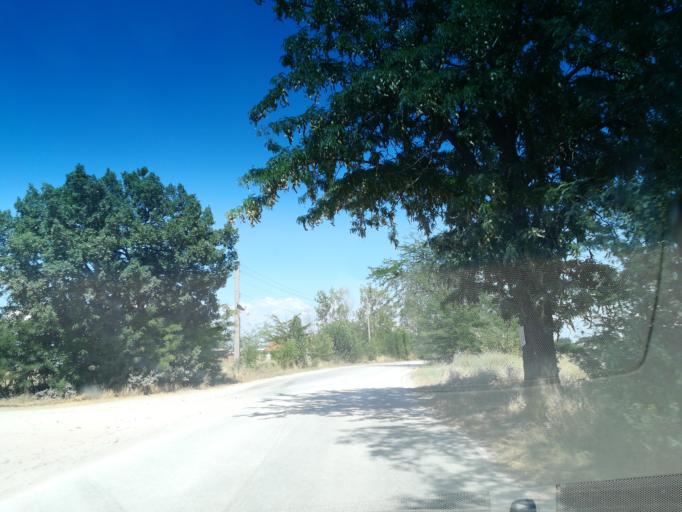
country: BG
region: Plovdiv
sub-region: Obshtina Sadovo
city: Sadovo
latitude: 42.0216
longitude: 25.0909
